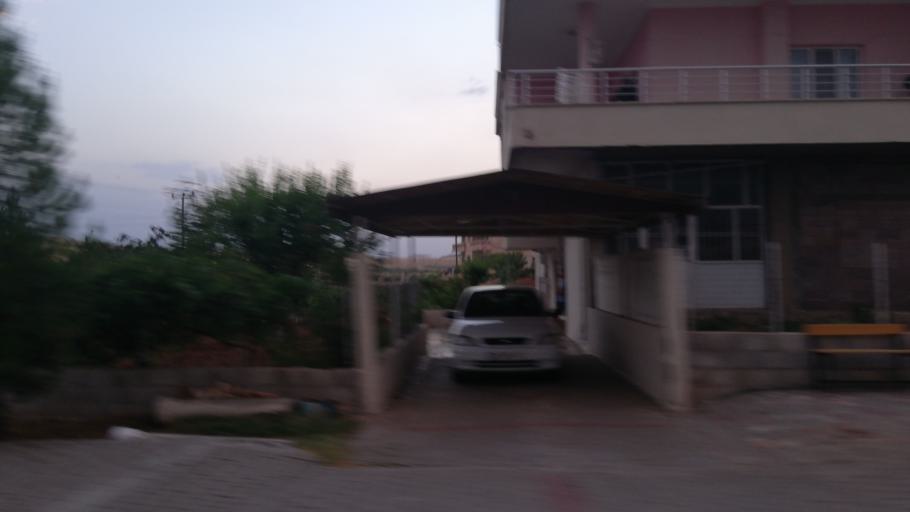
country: TR
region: Mardin
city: Kindirip
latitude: 37.4597
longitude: 41.2247
